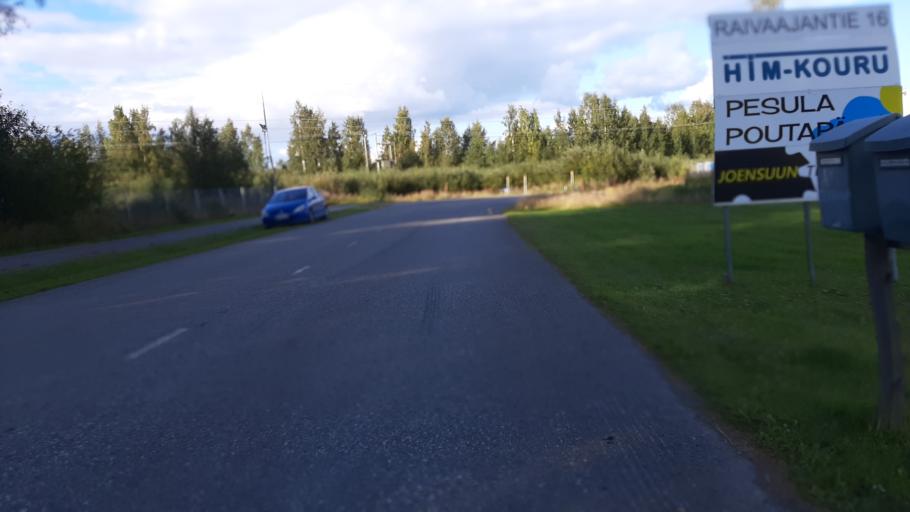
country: FI
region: North Karelia
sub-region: Joensuu
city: Joensuu
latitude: 62.6294
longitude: 29.8025
